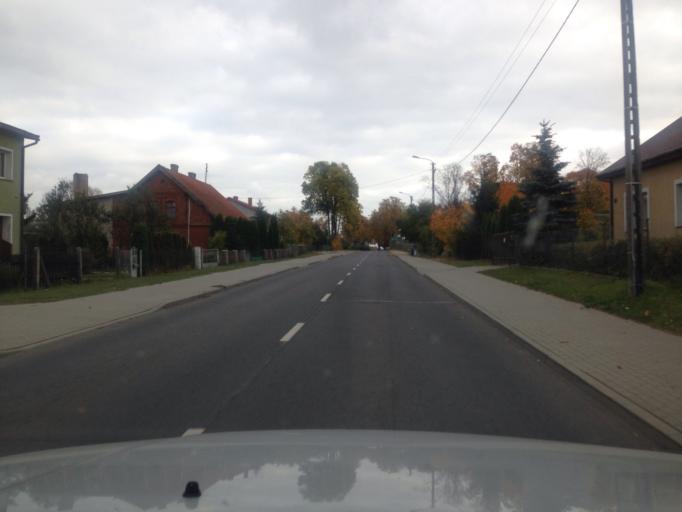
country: PL
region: Warmian-Masurian Voivodeship
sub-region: Powiat ostrodzki
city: Gierzwald
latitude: 53.4969
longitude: 20.1315
